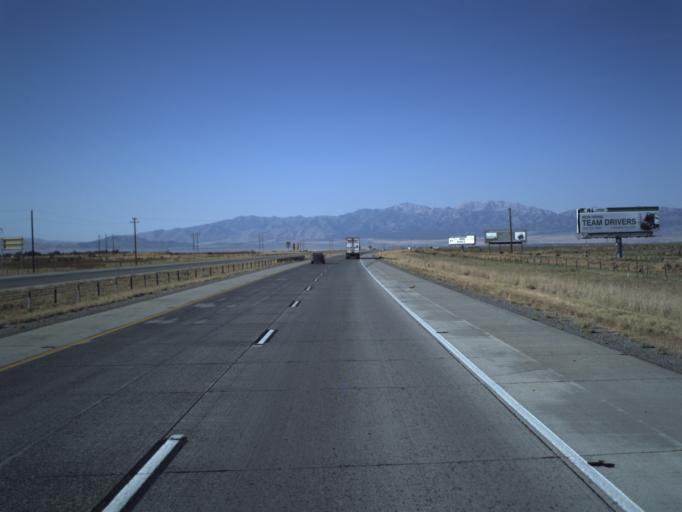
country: US
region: Utah
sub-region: Tooele County
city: Stansbury park
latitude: 40.6821
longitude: -112.2763
